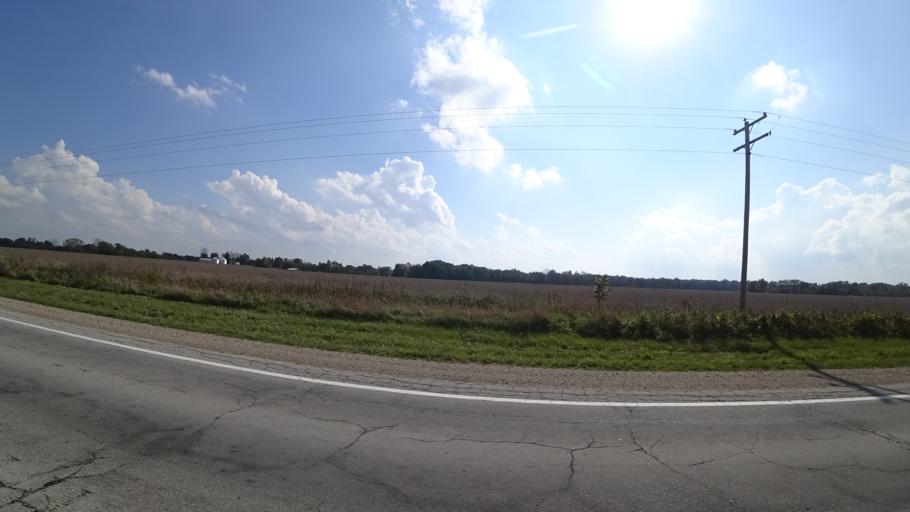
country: US
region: Michigan
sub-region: Saint Joseph County
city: Colon
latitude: 42.0102
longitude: -85.3727
